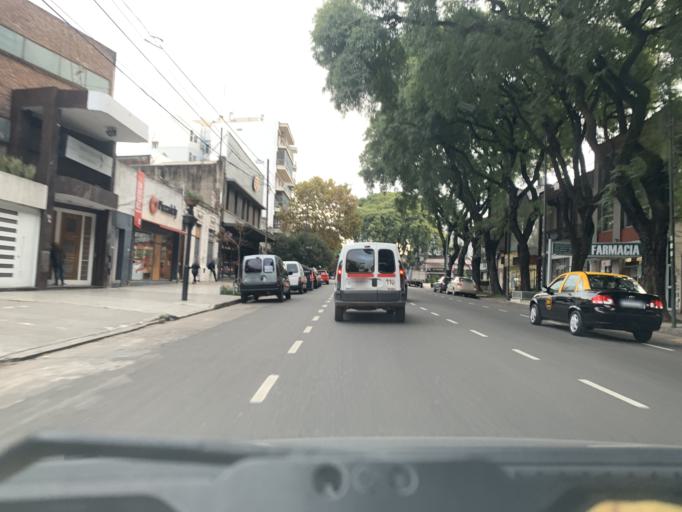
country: AR
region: Buenos Aires F.D.
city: Colegiales
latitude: -34.5785
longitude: -58.4637
